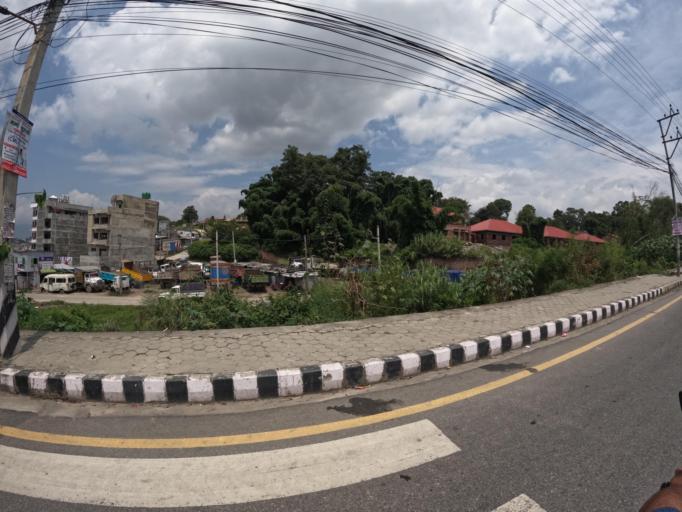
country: NP
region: Central Region
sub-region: Bagmati Zone
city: Kathmandu
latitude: 27.6829
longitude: 85.3701
